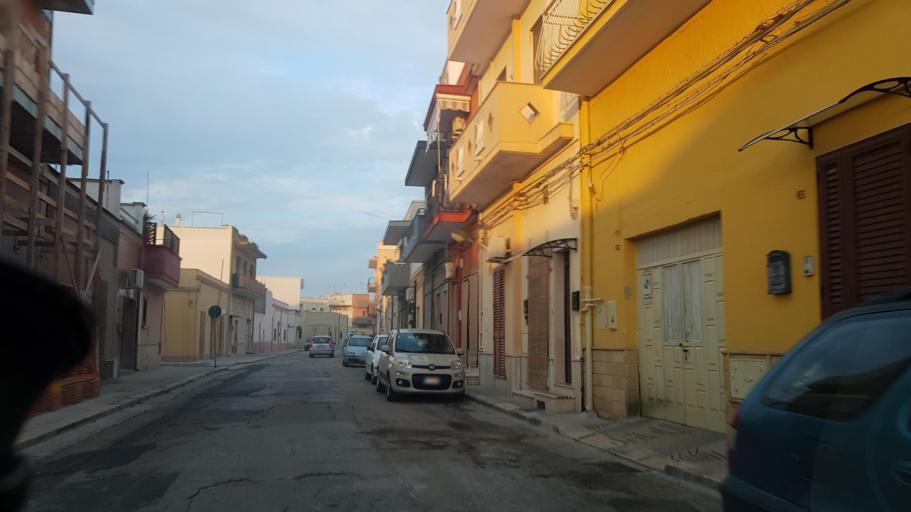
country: IT
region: Apulia
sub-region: Provincia di Brindisi
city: Mesagne
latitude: 40.5548
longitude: 17.8050
